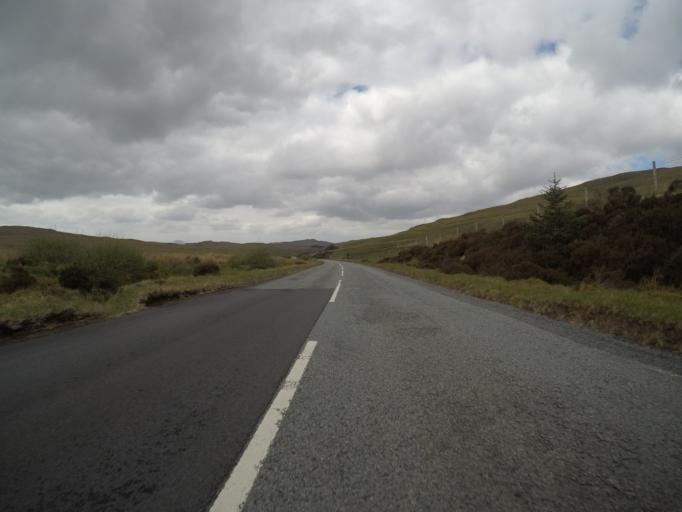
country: GB
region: Scotland
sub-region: Highland
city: Isle of Skye
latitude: 57.3195
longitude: -6.3237
